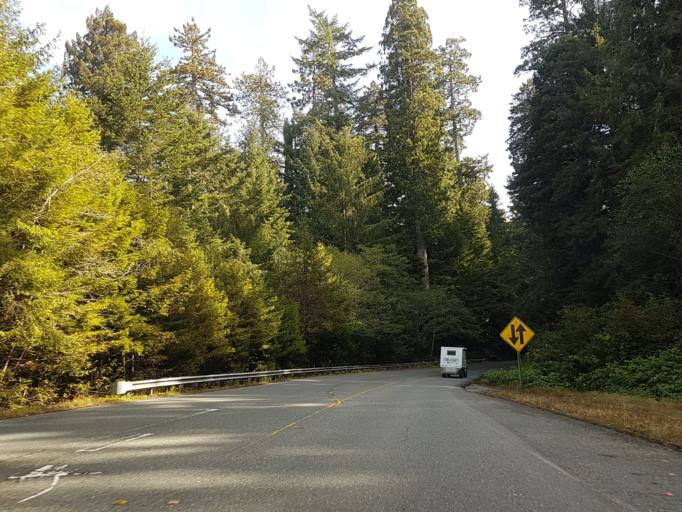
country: US
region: California
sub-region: Del Norte County
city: Bertsch-Oceanview
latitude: 41.4573
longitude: -124.0452
